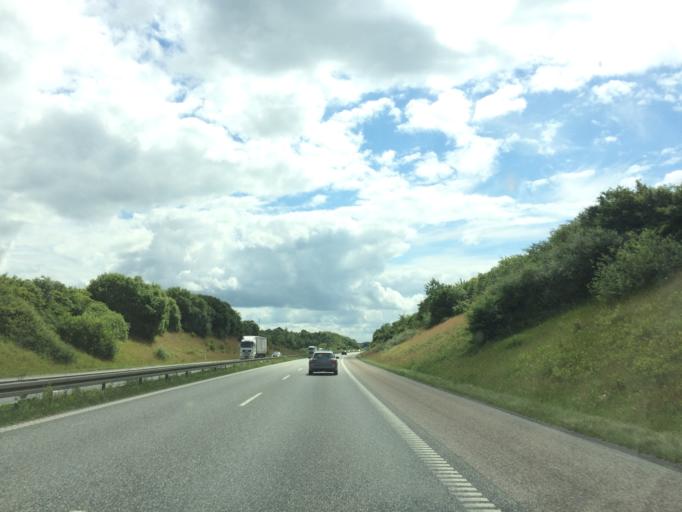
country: DK
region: North Denmark
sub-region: Mariagerfjord Kommune
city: Hobro
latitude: 56.7075
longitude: 9.7290
